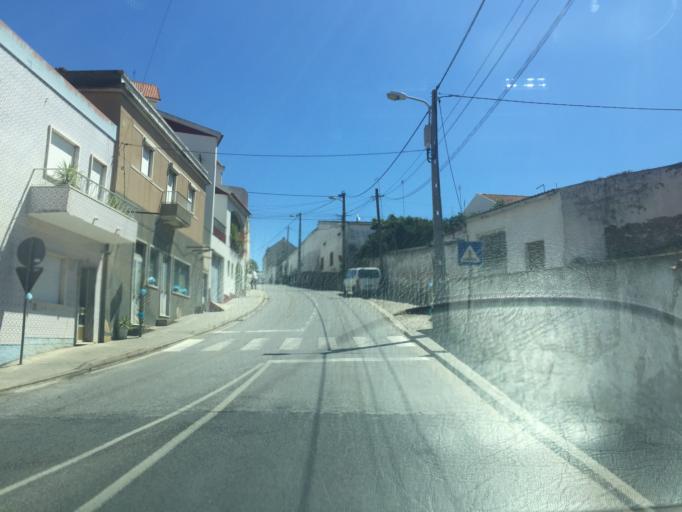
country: PT
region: Lisbon
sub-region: Torres Vedras
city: A dos Cunhados
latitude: 39.1829
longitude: -9.3297
